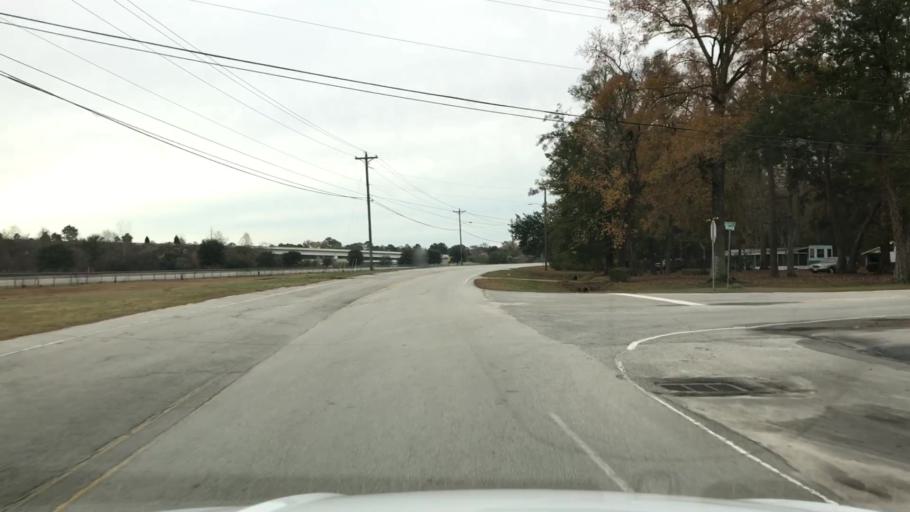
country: US
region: South Carolina
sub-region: Berkeley County
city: Goose Creek
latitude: 32.9720
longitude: -80.0505
